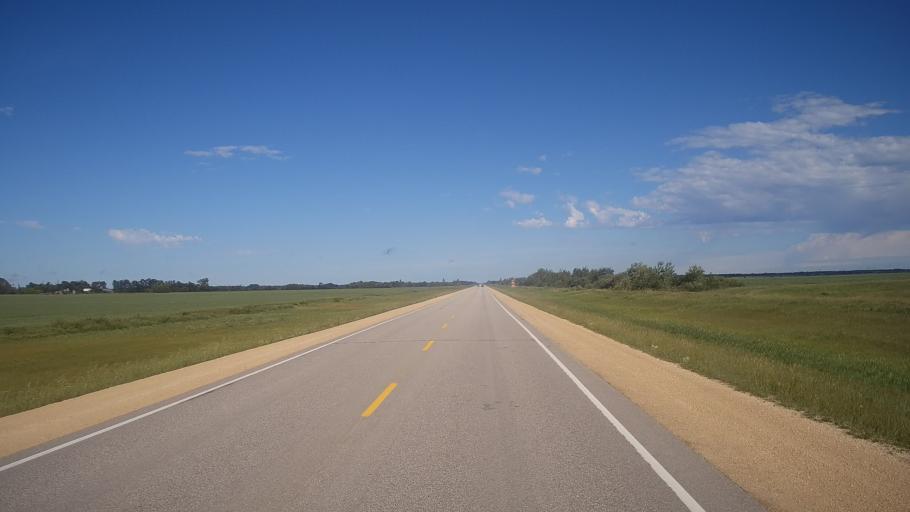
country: CA
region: Manitoba
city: Stonewall
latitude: 50.1845
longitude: -97.6274
